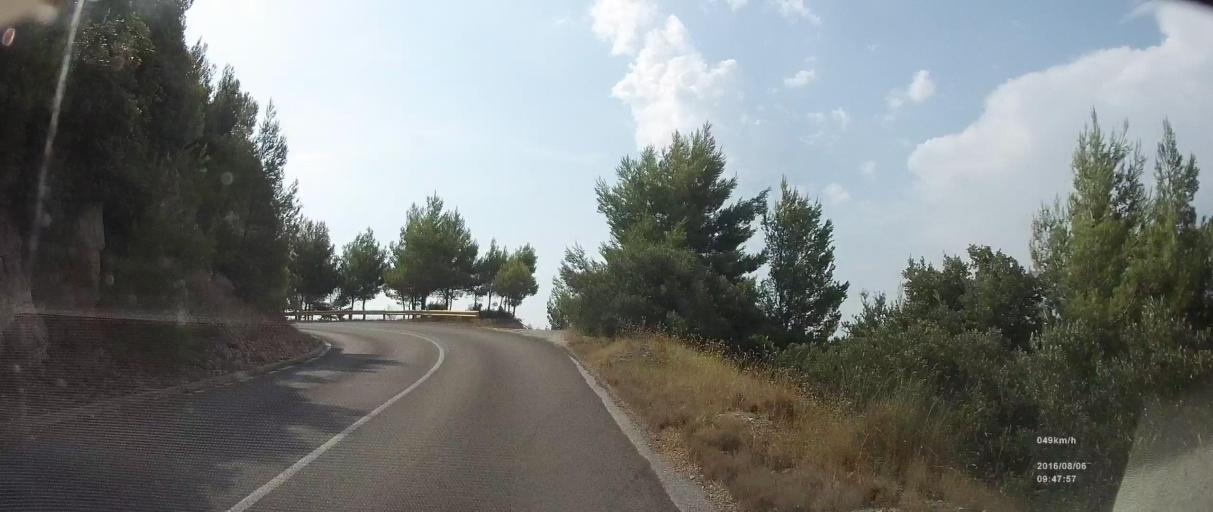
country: HR
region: Dubrovacko-Neretvanska
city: Blato
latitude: 42.7381
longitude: 17.5310
